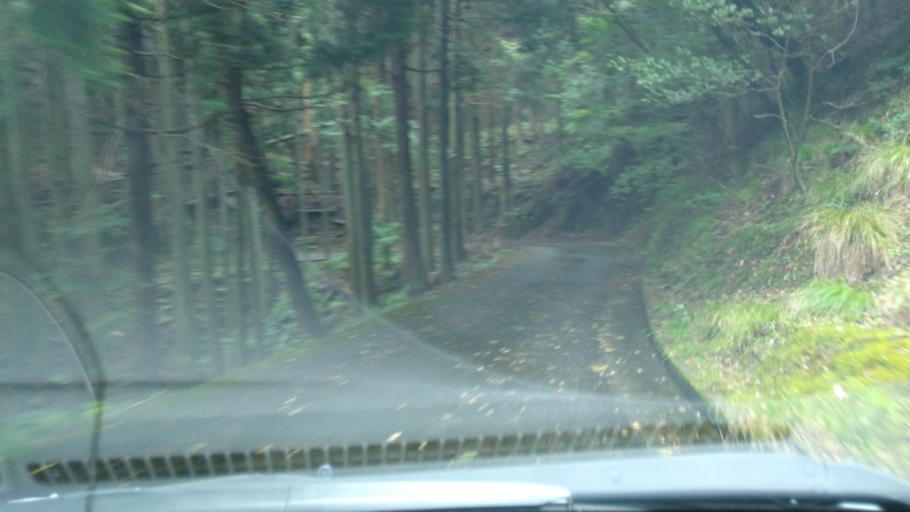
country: JP
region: Kyoto
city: Ayabe
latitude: 35.2280
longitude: 135.2771
